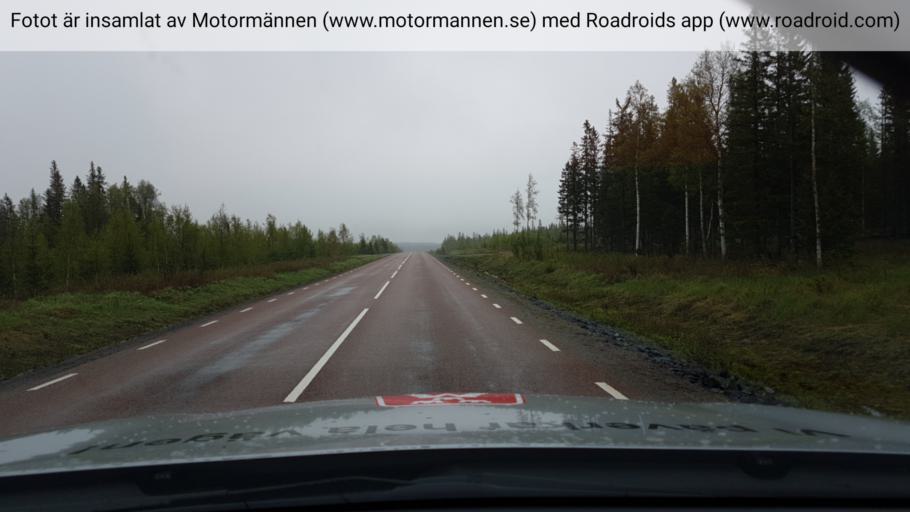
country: SE
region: Jaemtland
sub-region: Krokoms Kommun
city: Valla
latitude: 63.1403
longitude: 13.9437
